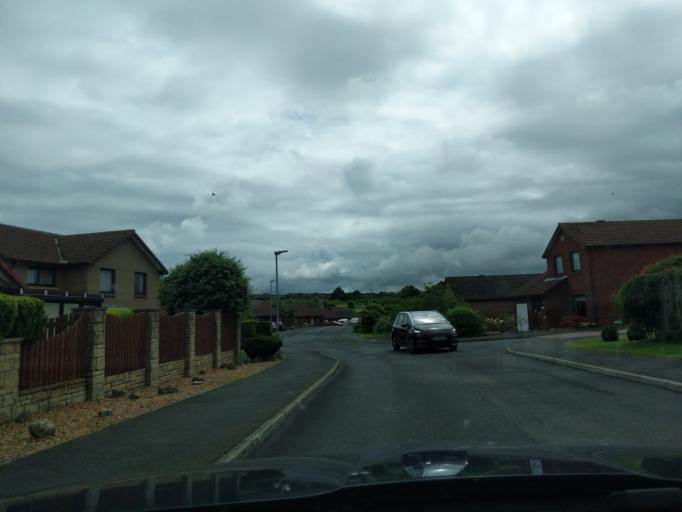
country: GB
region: England
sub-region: Northumberland
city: Berwick-Upon-Tweed
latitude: 55.7549
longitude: -2.0195
